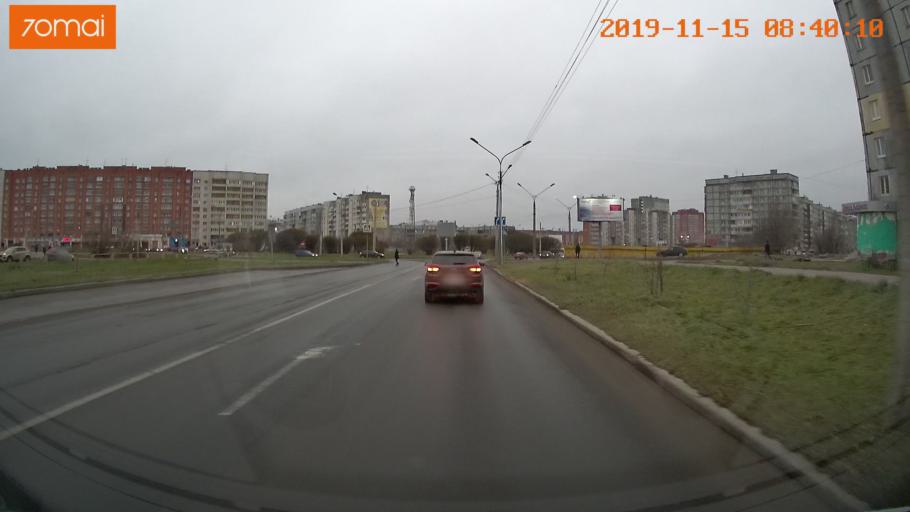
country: RU
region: Vologda
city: Cherepovets
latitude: 59.0939
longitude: 37.9169
